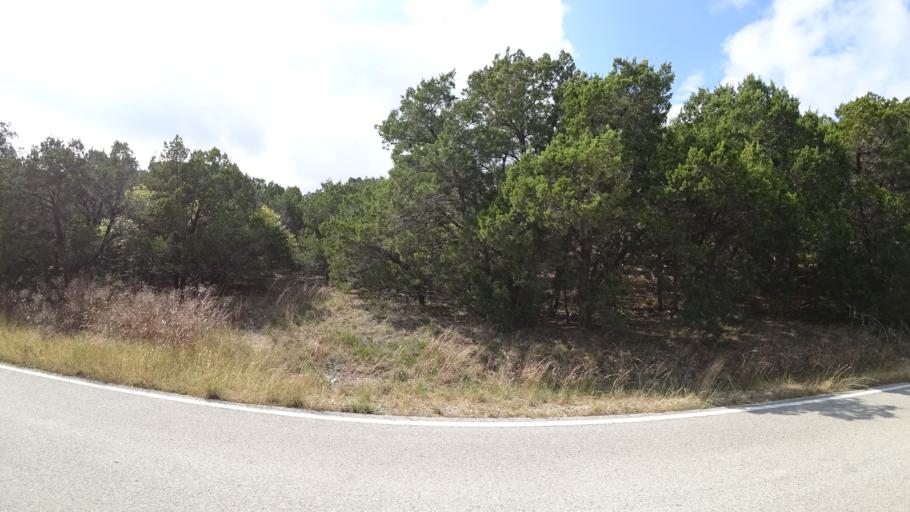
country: US
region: Texas
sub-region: Travis County
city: Barton Creek
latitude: 30.3033
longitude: -97.8735
